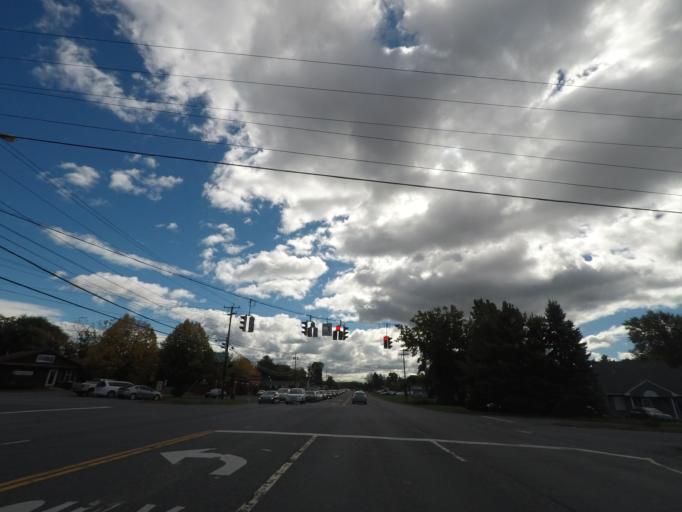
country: US
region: New York
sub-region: Saratoga County
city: Waterford
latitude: 42.8415
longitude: -73.7458
